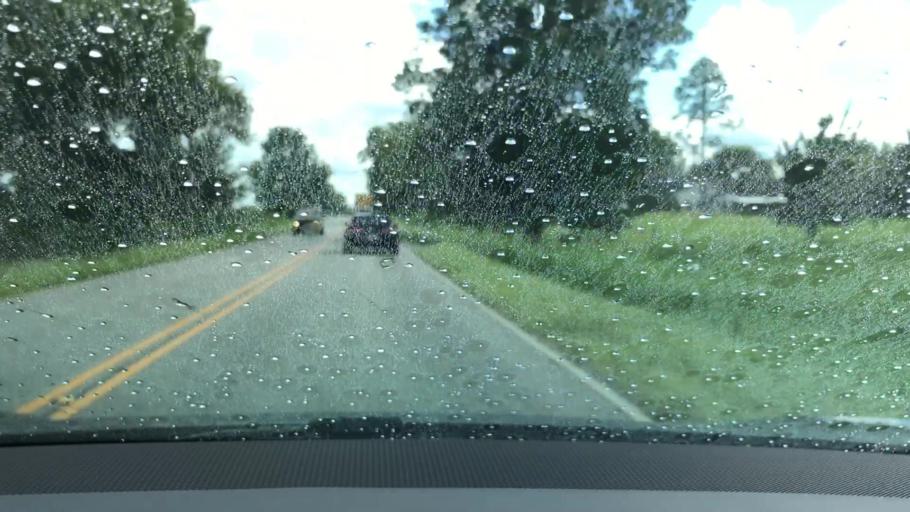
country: US
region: Alabama
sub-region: Montgomery County
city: Pike Road
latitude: 32.2431
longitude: -86.0932
